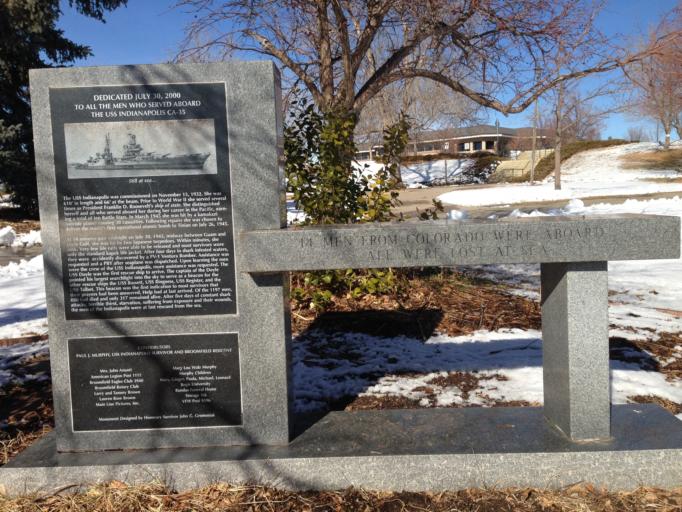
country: US
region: Colorado
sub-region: Broomfield County
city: Broomfield
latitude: 39.9186
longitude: -105.0684
